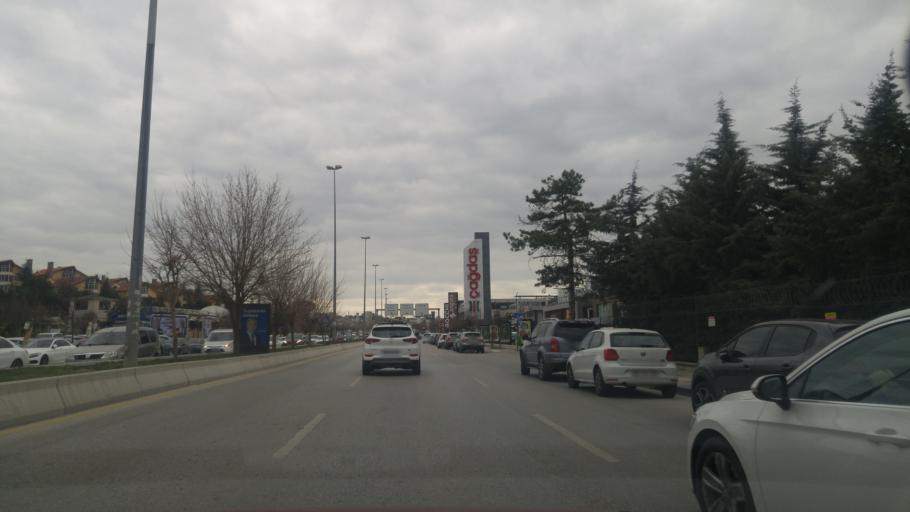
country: TR
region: Ankara
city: Etimesgut
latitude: 39.8707
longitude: 32.6869
